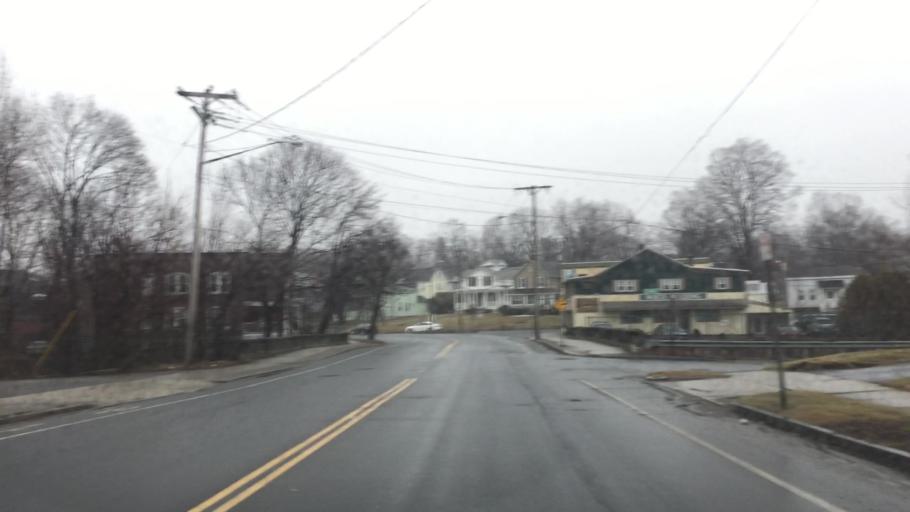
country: US
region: Massachusetts
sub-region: Berkshire County
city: Pittsfield
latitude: 42.4456
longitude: -73.2443
